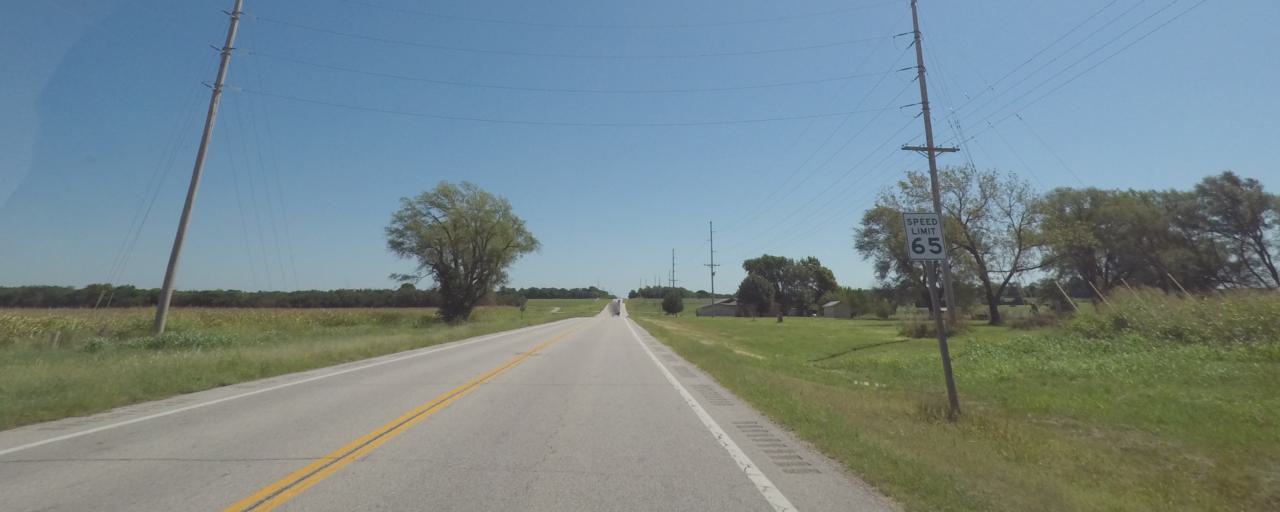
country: US
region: Kansas
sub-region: Sumner County
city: Belle Plaine
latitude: 37.3912
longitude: -97.3817
